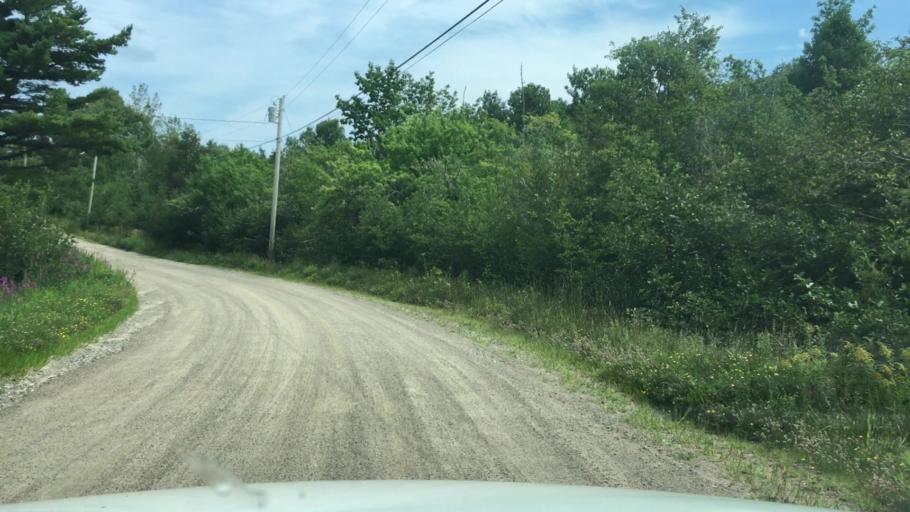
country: CA
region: New Brunswick
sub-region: Charlotte County
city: Saint Andrews
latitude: 45.0350
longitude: -67.1137
